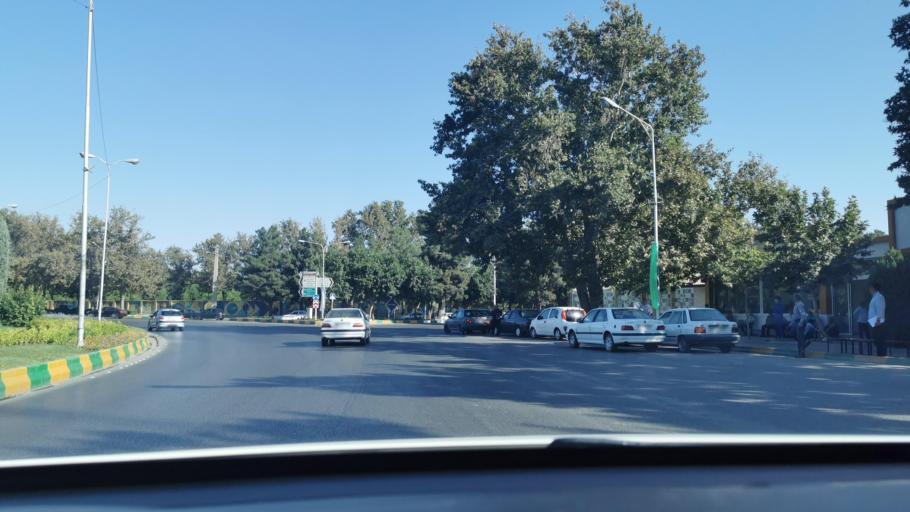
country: IR
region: Razavi Khorasan
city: Mashhad
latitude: 36.3242
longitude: 59.5788
